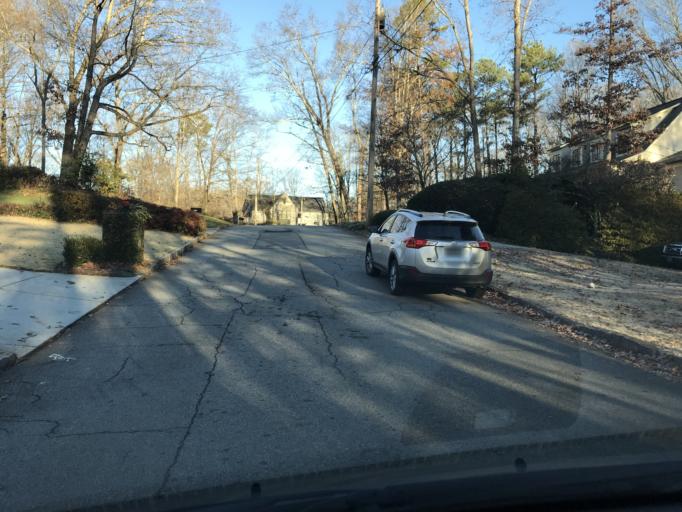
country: US
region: Georgia
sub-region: DeKalb County
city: North Atlanta
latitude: 33.8824
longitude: -84.3355
